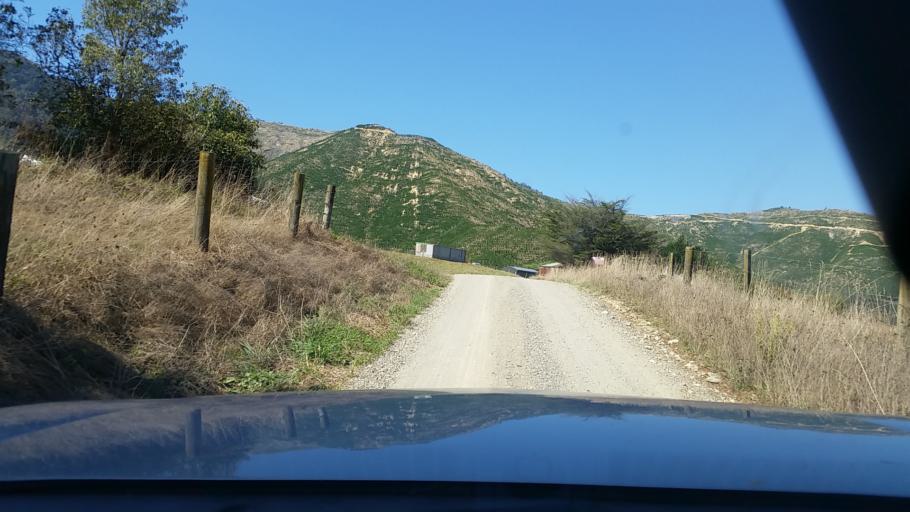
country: NZ
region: Nelson
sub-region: Nelson City
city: Nelson
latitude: -41.2711
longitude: 173.5795
